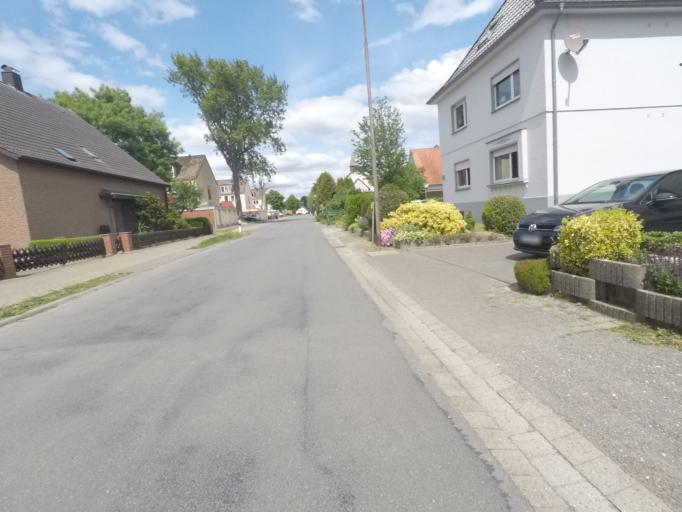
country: DE
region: North Rhine-Westphalia
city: Enger
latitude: 52.1567
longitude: 8.5808
